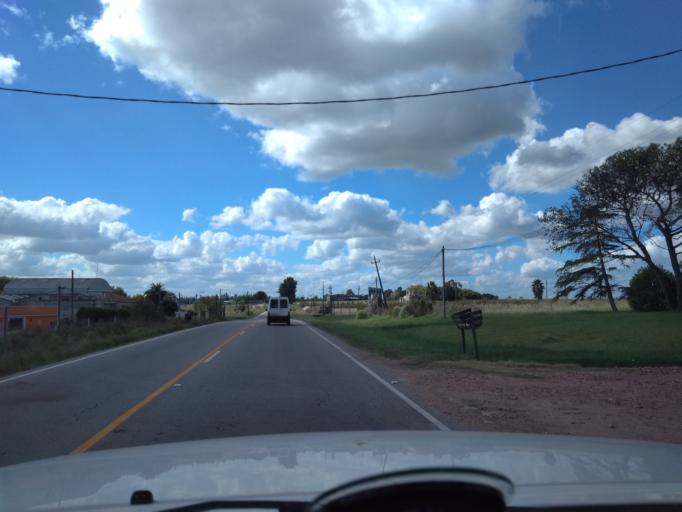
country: UY
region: Canelones
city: Joaquin Suarez
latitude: -34.6924
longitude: -56.0550
